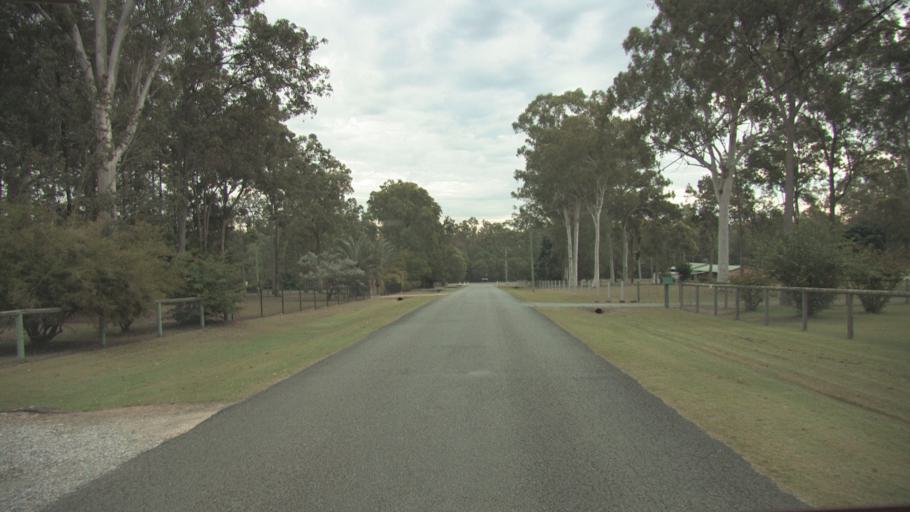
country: AU
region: Queensland
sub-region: Logan
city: Chambers Flat
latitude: -27.7871
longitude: 153.1102
